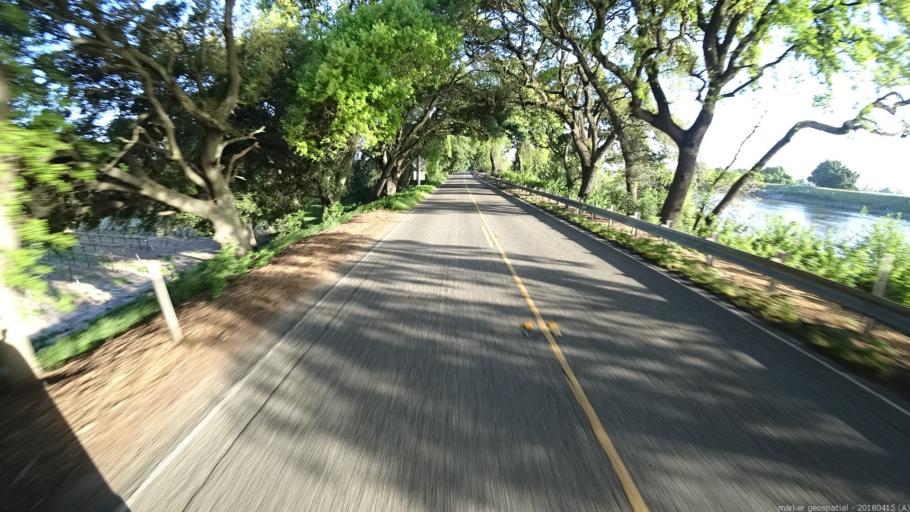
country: US
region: California
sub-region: Sacramento County
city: Walnut Grove
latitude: 38.3083
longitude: -121.5764
